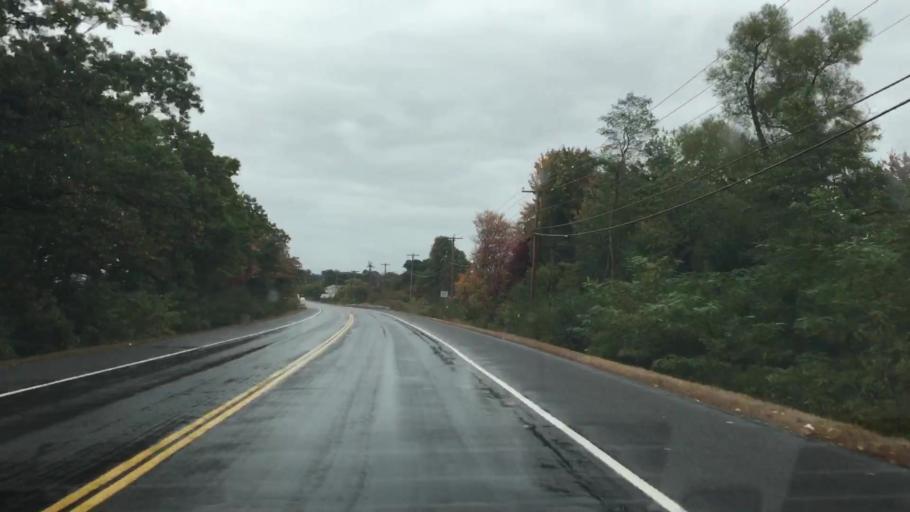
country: US
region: Massachusetts
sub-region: Essex County
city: Salisbury
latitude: 42.8697
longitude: -70.8429
